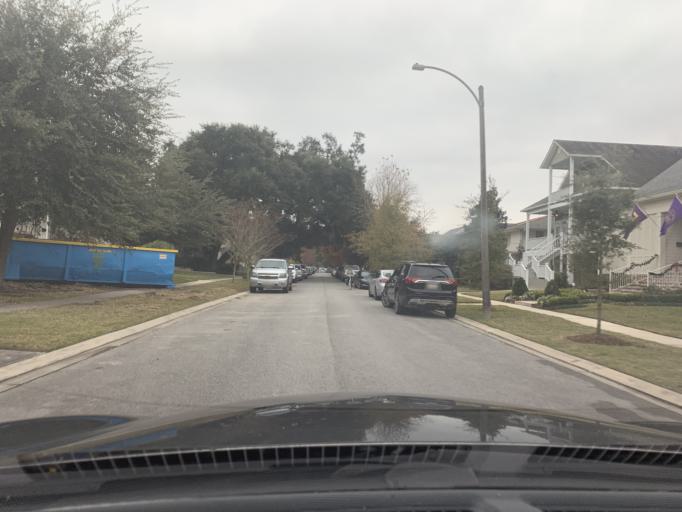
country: US
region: Louisiana
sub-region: Jefferson Parish
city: Metairie
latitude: 30.0174
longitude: -90.1089
